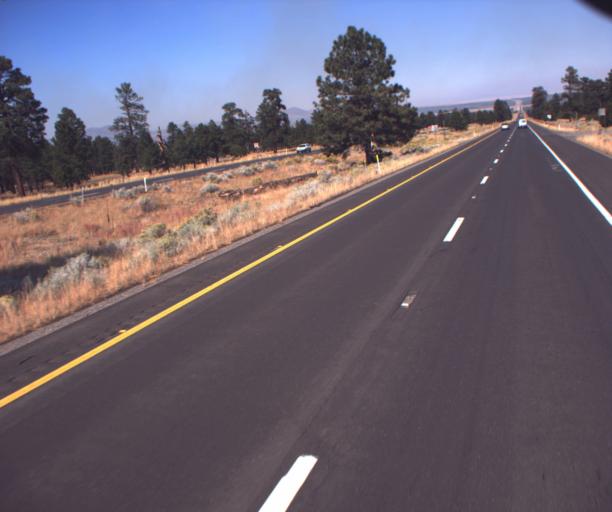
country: US
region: Arizona
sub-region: Coconino County
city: Flagstaff
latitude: 35.3895
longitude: -111.5787
